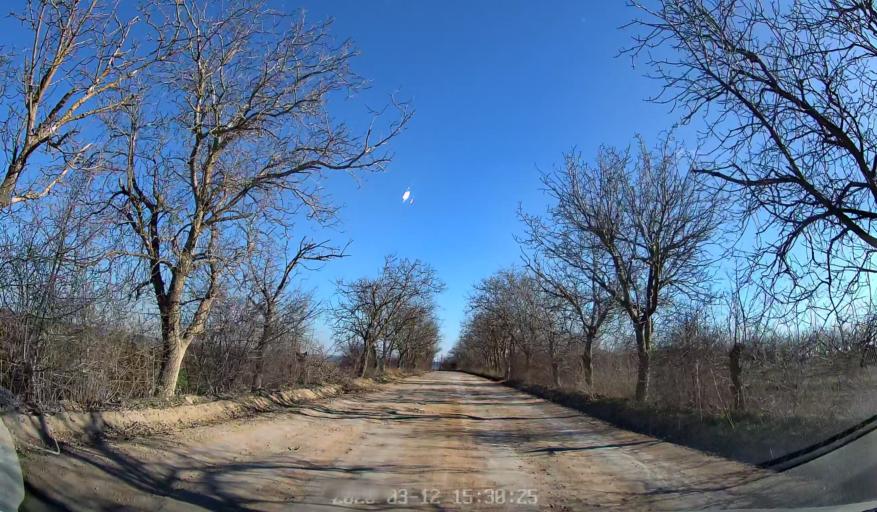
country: MD
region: Chisinau
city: Ciorescu
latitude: 47.1610
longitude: 28.9388
